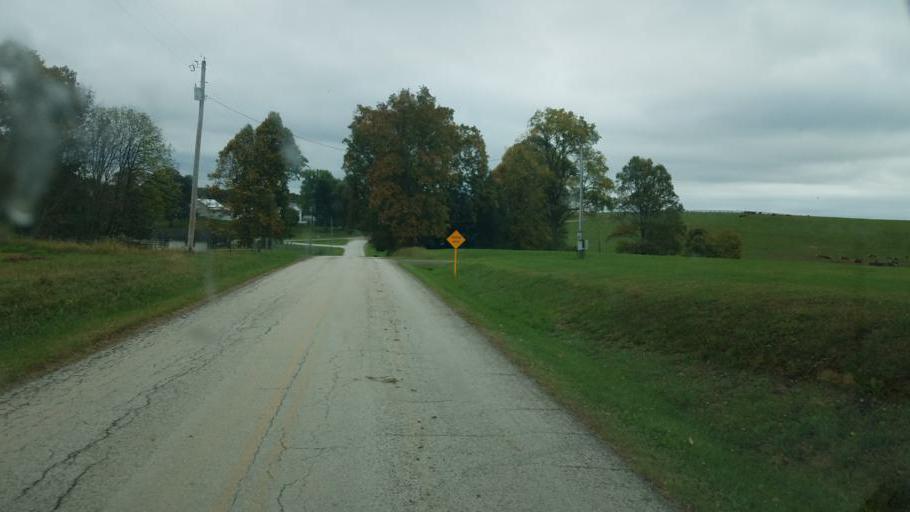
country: US
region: Ohio
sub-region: Ashland County
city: Loudonville
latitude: 40.5628
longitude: -82.1630
